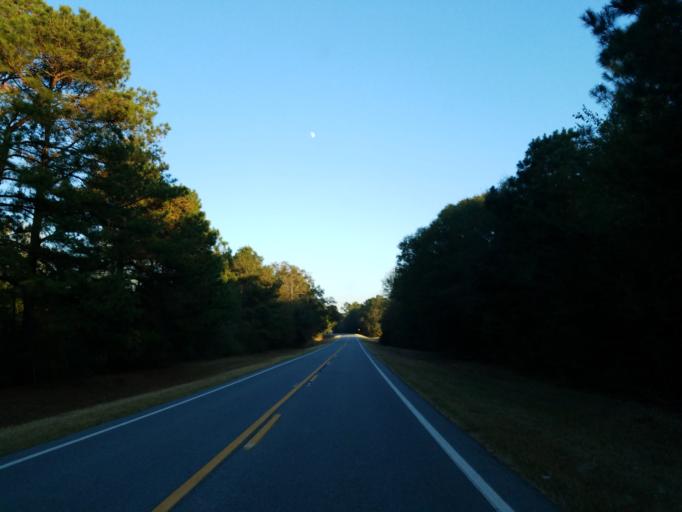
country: US
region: Georgia
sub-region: Wilcox County
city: Rochelle
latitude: 31.8149
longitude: -83.5077
